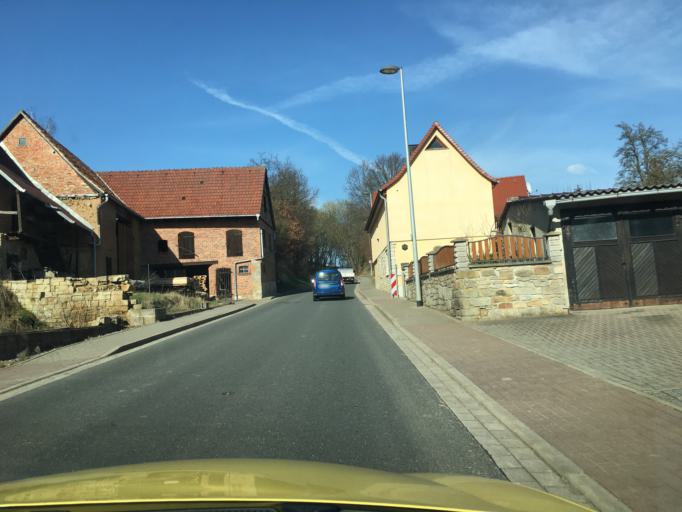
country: DE
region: Thuringia
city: Rastenberg
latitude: 51.2020
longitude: 11.4253
